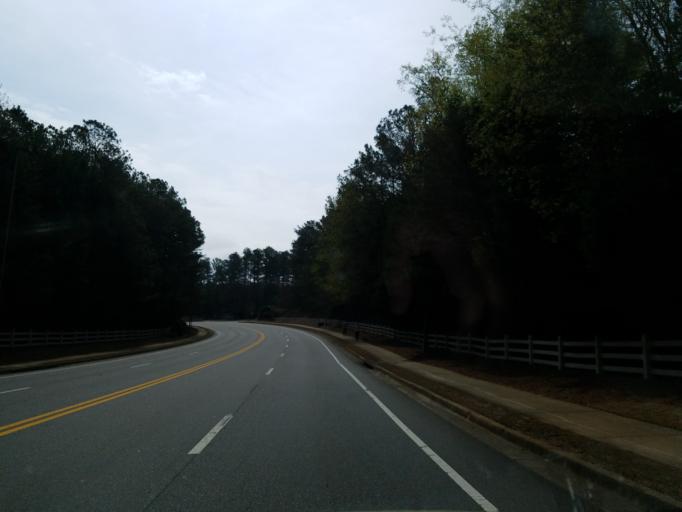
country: US
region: Georgia
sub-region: Fulton County
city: Johns Creek
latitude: 34.0936
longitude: -84.2162
